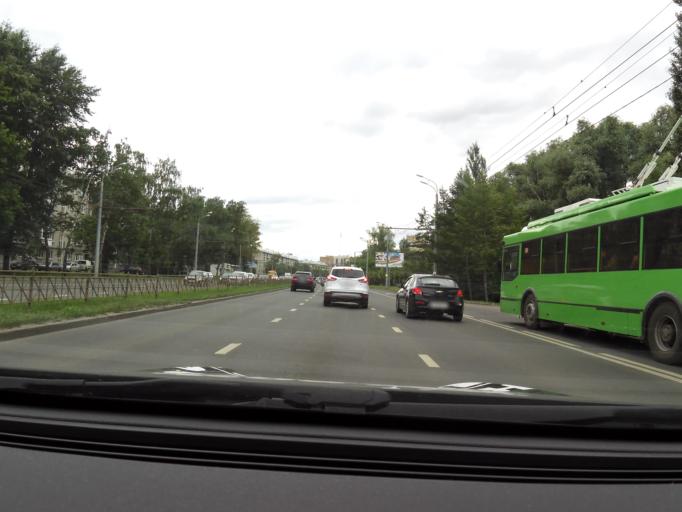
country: RU
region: Tatarstan
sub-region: Gorod Kazan'
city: Kazan
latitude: 55.8177
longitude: 49.0618
